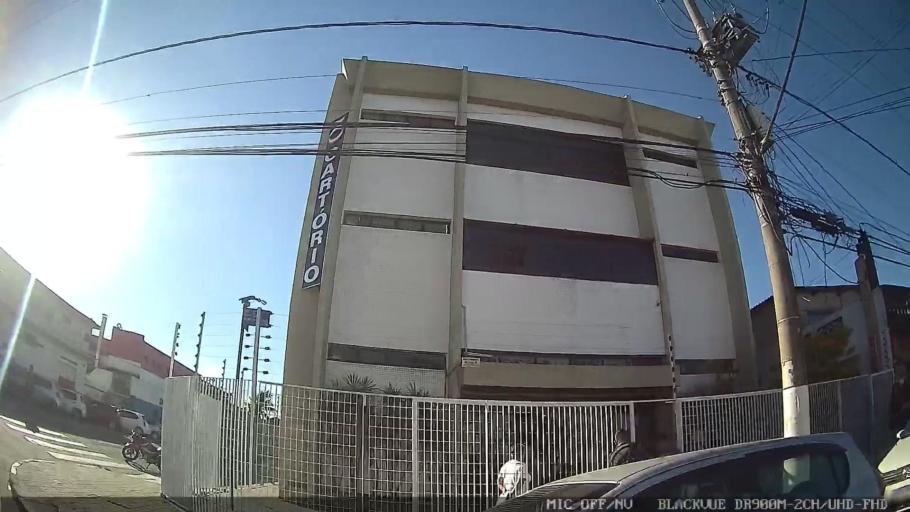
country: BR
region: Sao Paulo
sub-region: Santos
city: Santos
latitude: -23.9568
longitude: -46.2922
